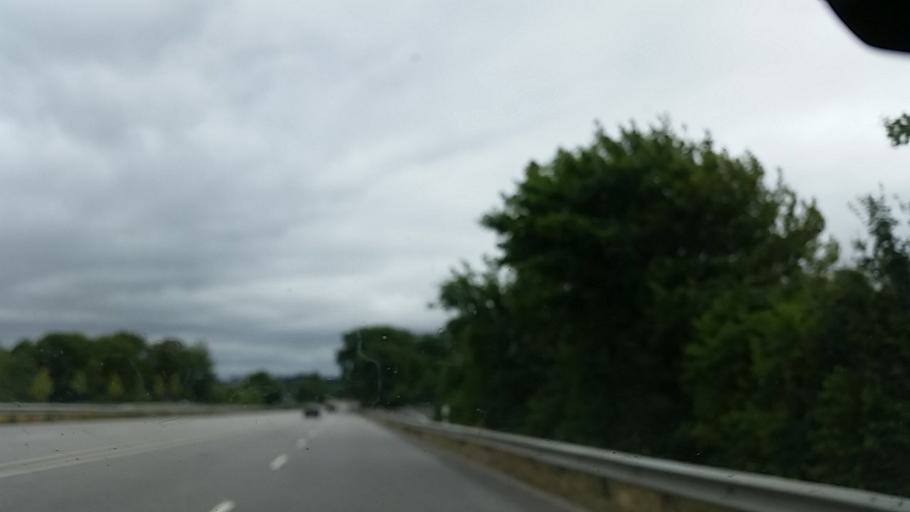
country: DE
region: Schleswig-Holstein
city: Windeby
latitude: 54.4765
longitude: 9.8226
